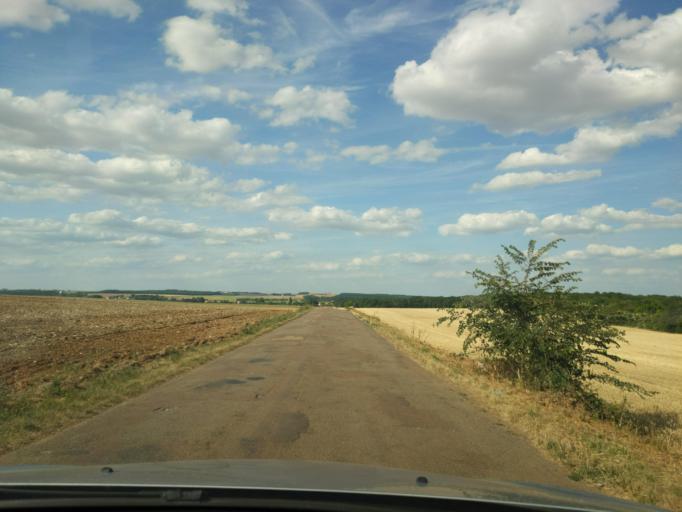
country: FR
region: Bourgogne
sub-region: Departement de la Cote-d'Or
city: Ruffey-les-Echirey
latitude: 47.3891
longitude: 5.0774
